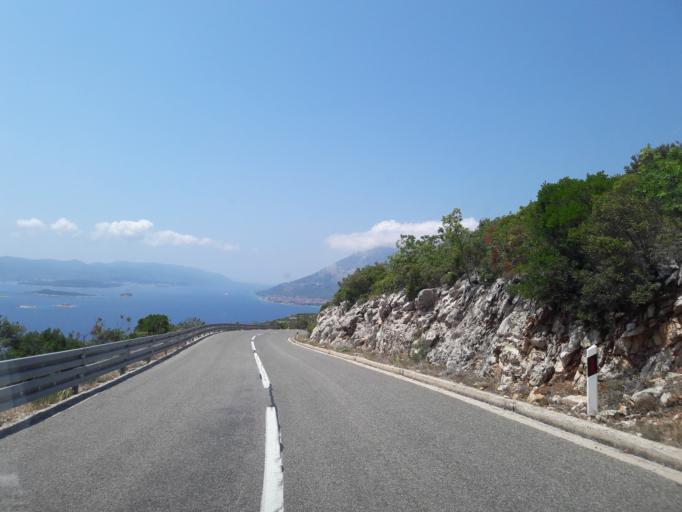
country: HR
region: Dubrovacko-Neretvanska
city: Orebic
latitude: 42.9701
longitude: 17.2494
